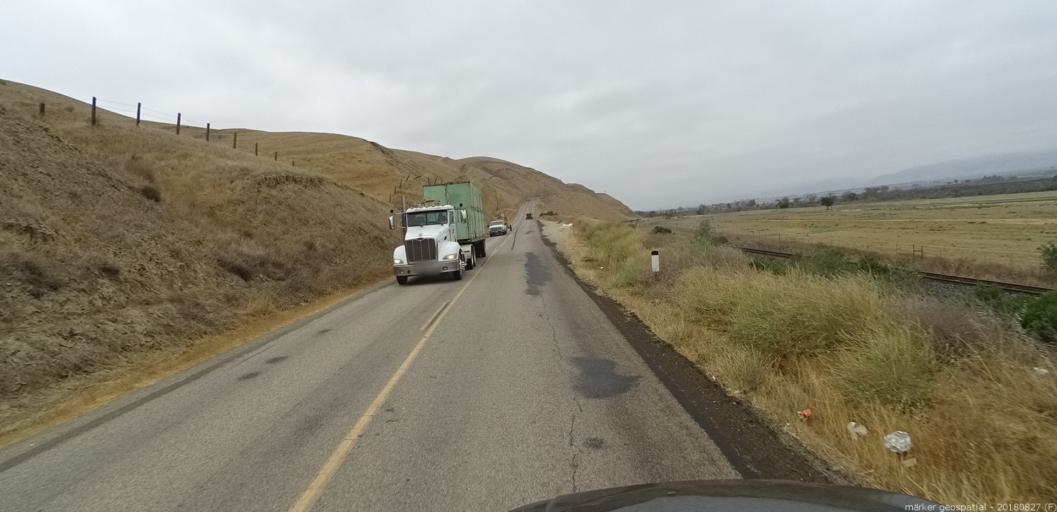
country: US
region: California
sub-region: Monterey County
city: Greenfield
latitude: 36.3256
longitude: -121.1840
